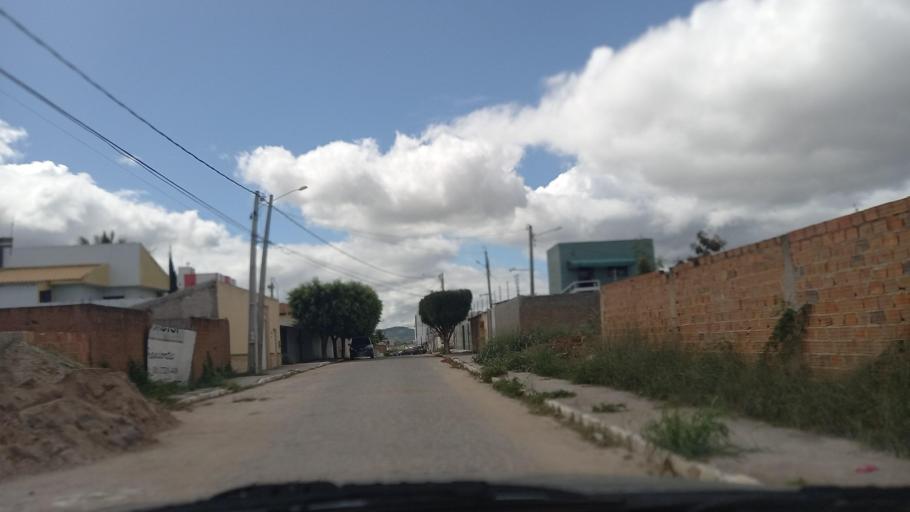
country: BR
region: Pernambuco
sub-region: Caruaru
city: Caruaru
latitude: -8.2576
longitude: -35.9805
